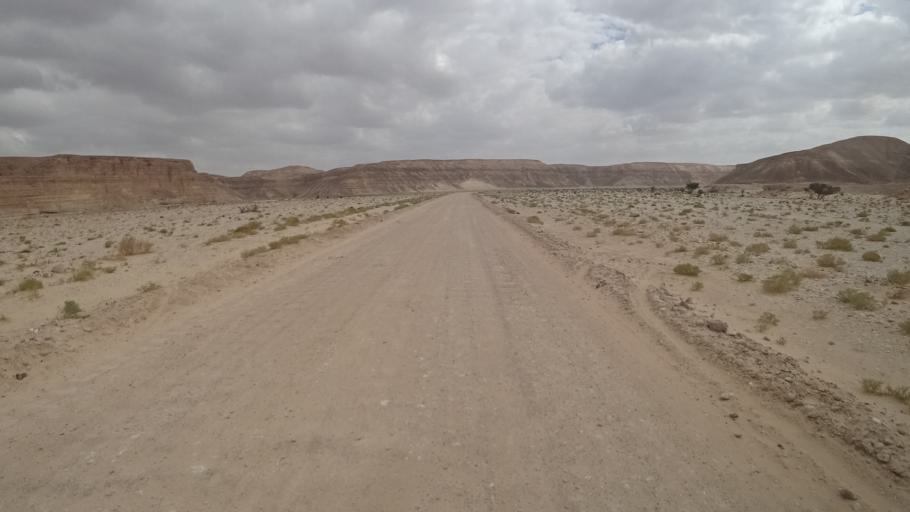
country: YE
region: Al Mahrah
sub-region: Shahan
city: Shihan as Sufla
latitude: 17.4717
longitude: 53.0017
